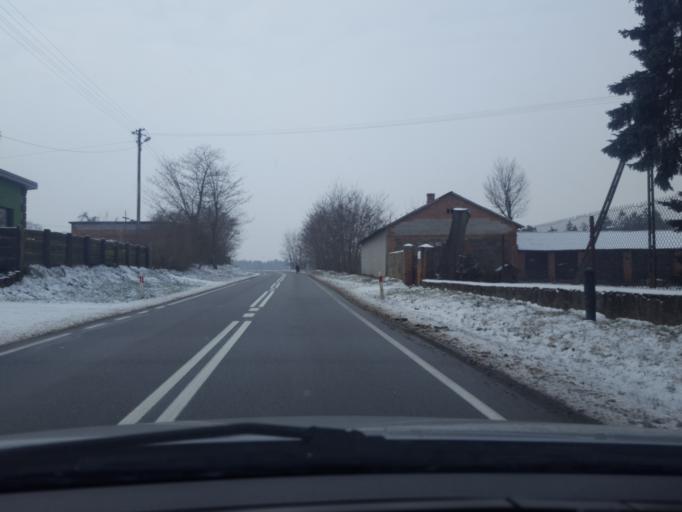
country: PL
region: Lodz Voivodeship
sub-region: Powiat brzezinski
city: Rogow
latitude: 51.8652
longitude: 19.8301
